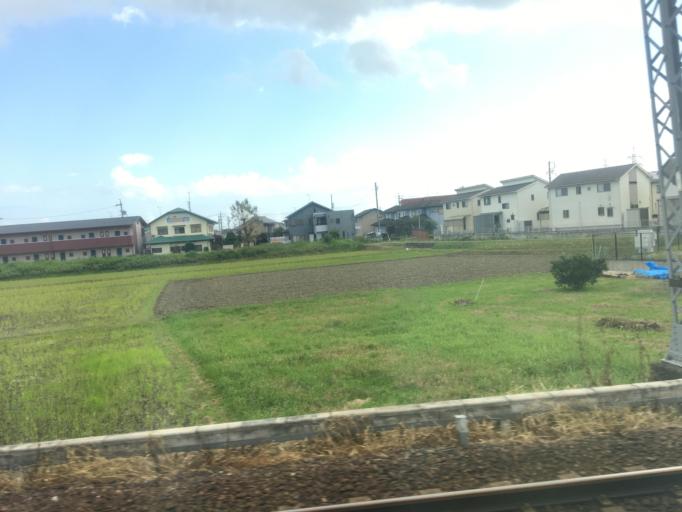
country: JP
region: Mie
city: Hisai-motomachi
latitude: 34.6378
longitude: 136.4765
